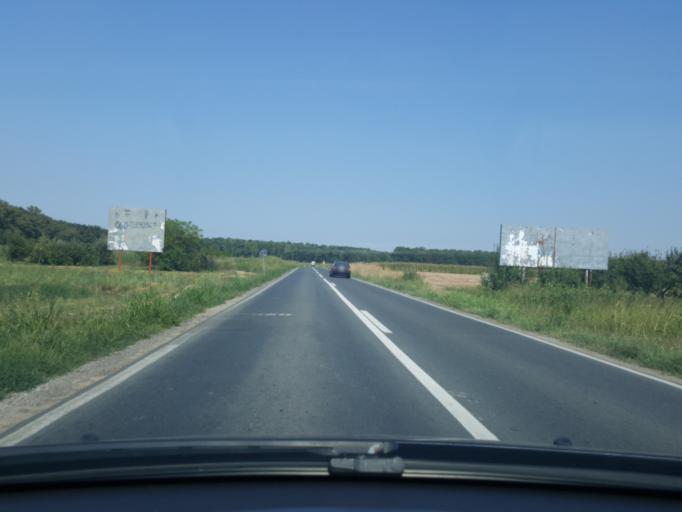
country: RS
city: Klenak
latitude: 44.8036
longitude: 19.7343
